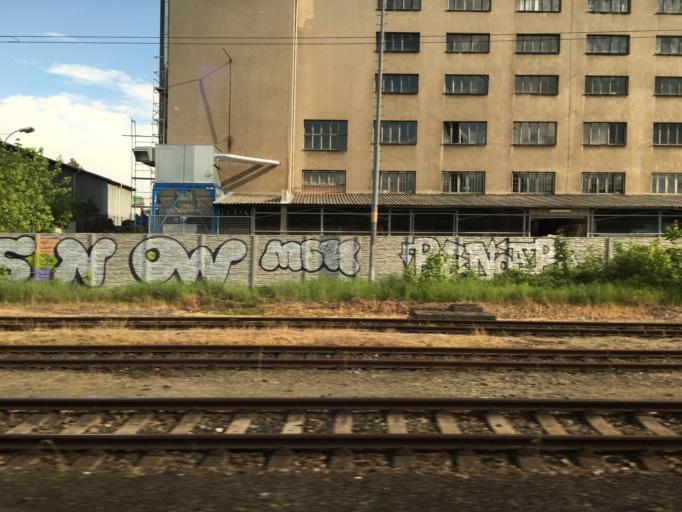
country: CZ
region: Ustecky
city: Roudnice nad Labem
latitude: 50.4285
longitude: 14.2806
